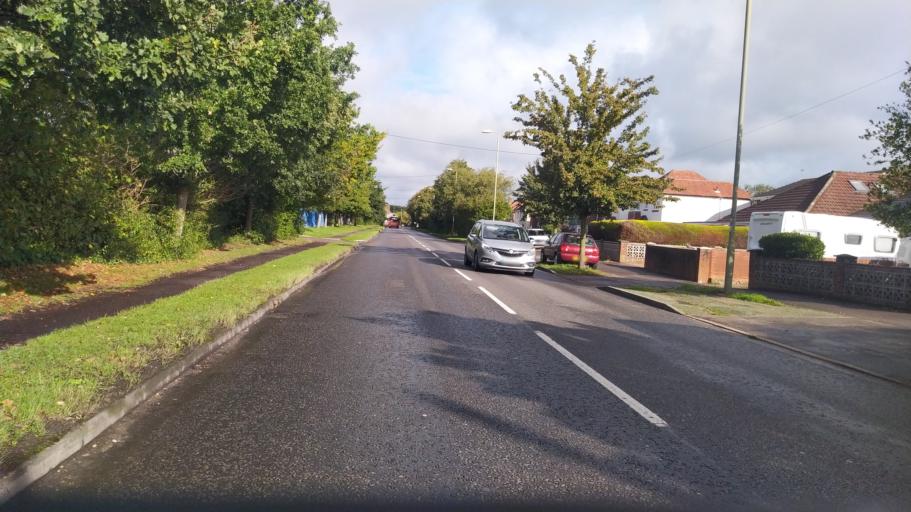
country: GB
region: England
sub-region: Hampshire
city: Totton
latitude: 50.9239
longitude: -1.4971
